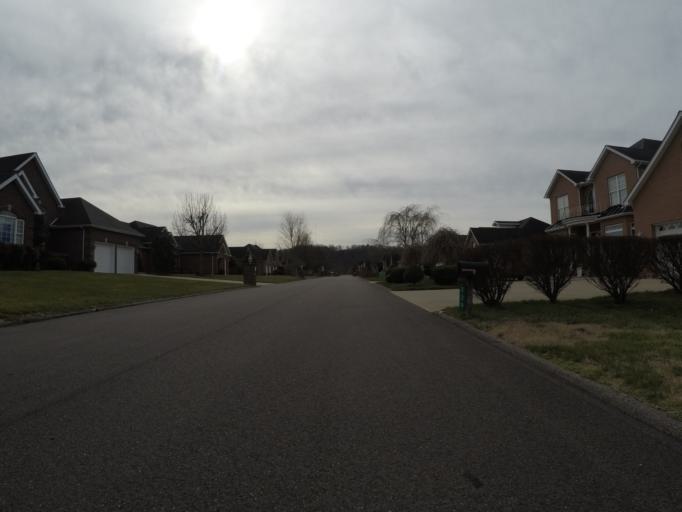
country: US
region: West Virginia
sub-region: Cabell County
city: Pea Ridge
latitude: 38.4468
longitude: -82.3485
